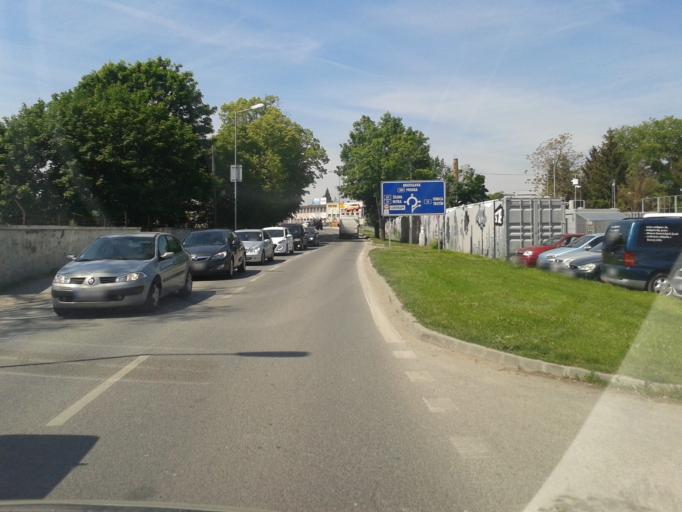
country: SK
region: Trnavsky
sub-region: Okres Trnava
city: Trnava
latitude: 48.3867
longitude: 17.5772
